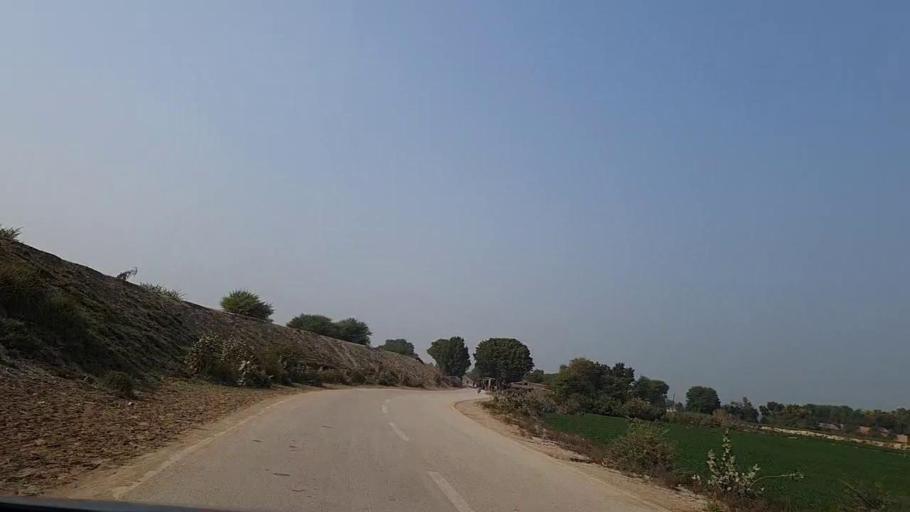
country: PK
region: Sindh
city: Sann
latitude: 26.1541
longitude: 68.1195
